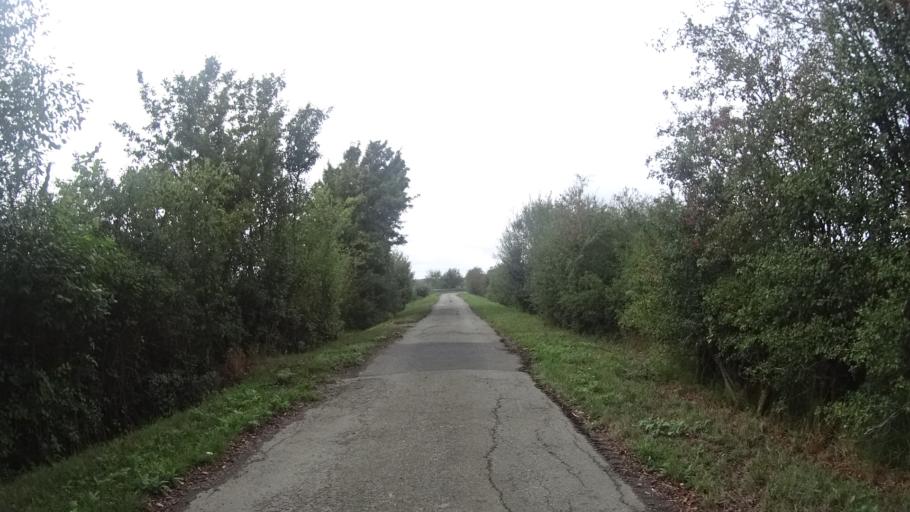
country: FR
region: Nord-Pas-de-Calais
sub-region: Departement du Nord
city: Maroilles
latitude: 50.1488
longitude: 3.7499
